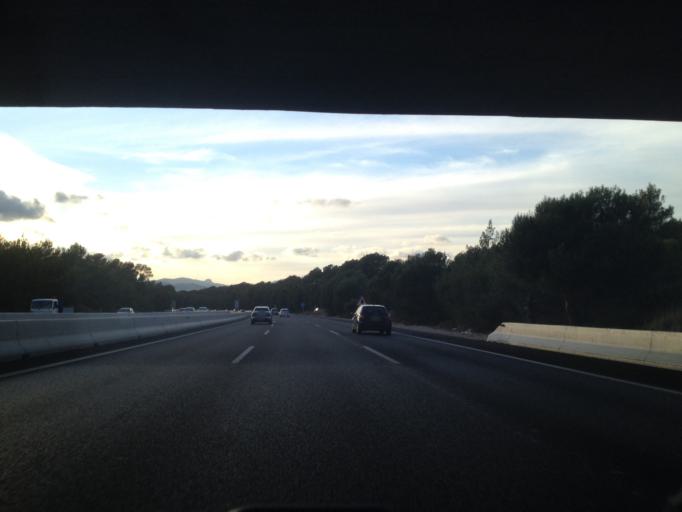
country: ES
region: Balearic Islands
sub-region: Illes Balears
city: Marratxi
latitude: 39.6301
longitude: 2.7263
